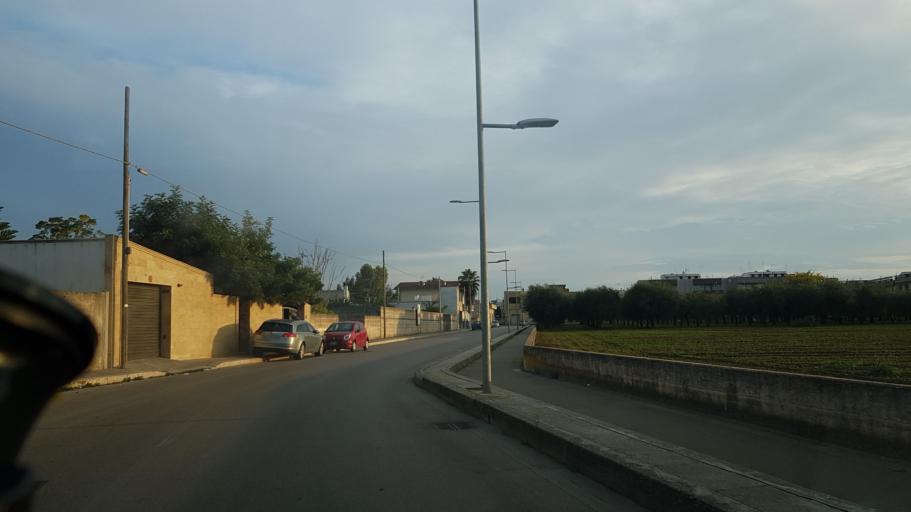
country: IT
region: Apulia
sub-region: Provincia di Brindisi
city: Latiano
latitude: 40.5565
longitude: 17.7237
